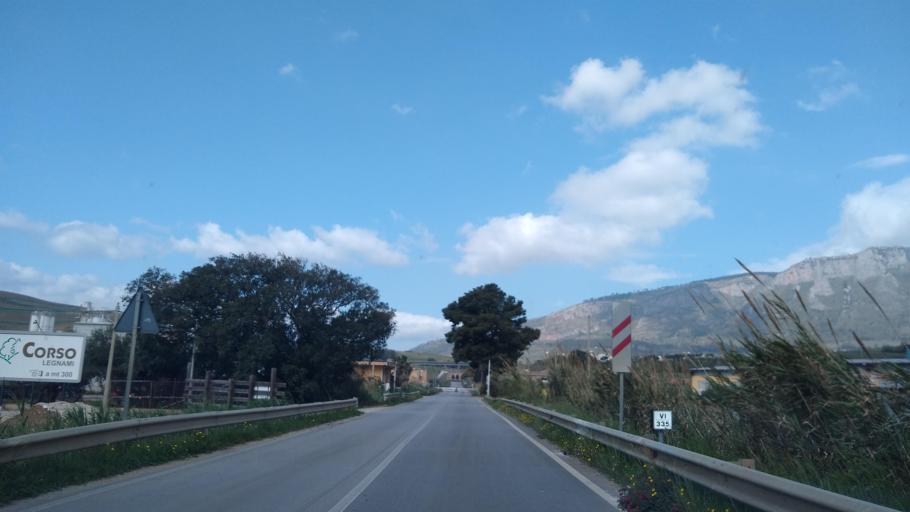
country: IT
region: Sicily
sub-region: Trapani
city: Alcamo
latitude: 37.9677
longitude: 12.9171
